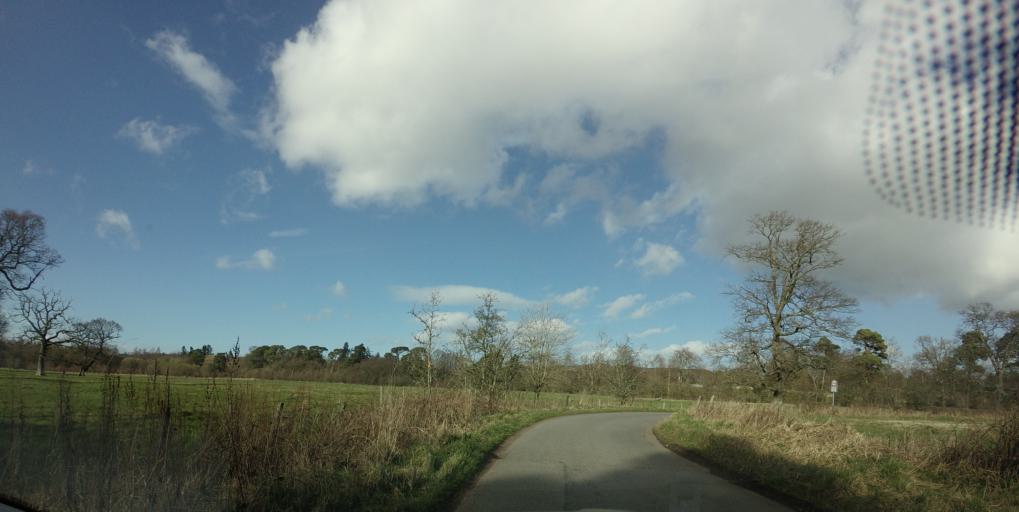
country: GB
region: Scotland
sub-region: Perth and Kinross
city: Bridge of Earn
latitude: 56.3377
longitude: -3.4270
